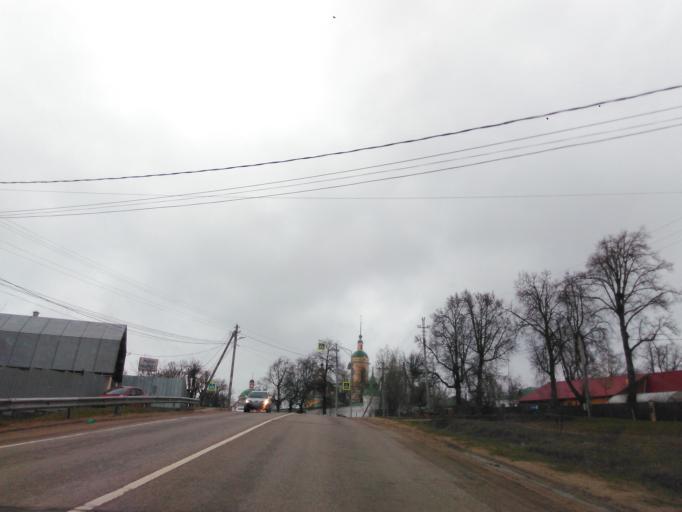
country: RU
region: Moskovskaya
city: Rozhdestveno
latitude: 55.8399
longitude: 37.0065
